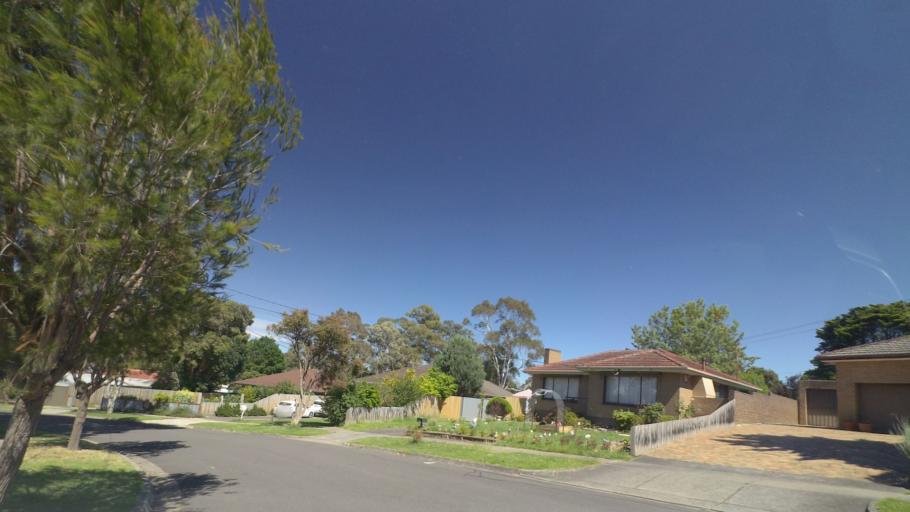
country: AU
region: Victoria
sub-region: Yarra Ranges
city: Kilsyth
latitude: -37.7964
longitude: 145.3216
